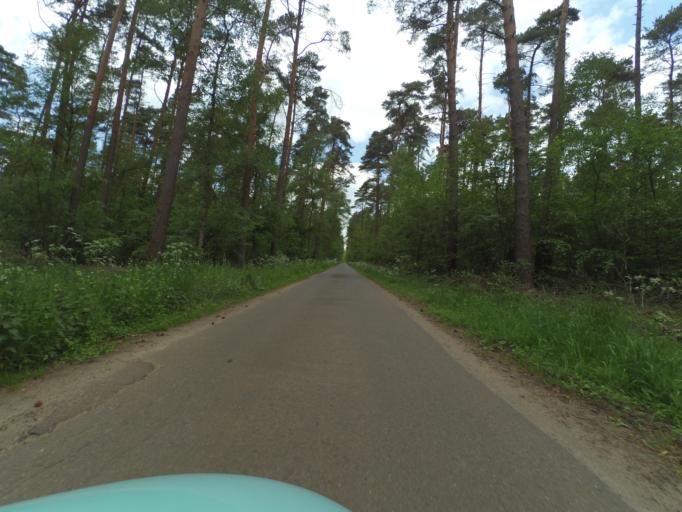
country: DE
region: Lower Saxony
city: Wietze
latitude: 52.6216
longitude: 9.8081
